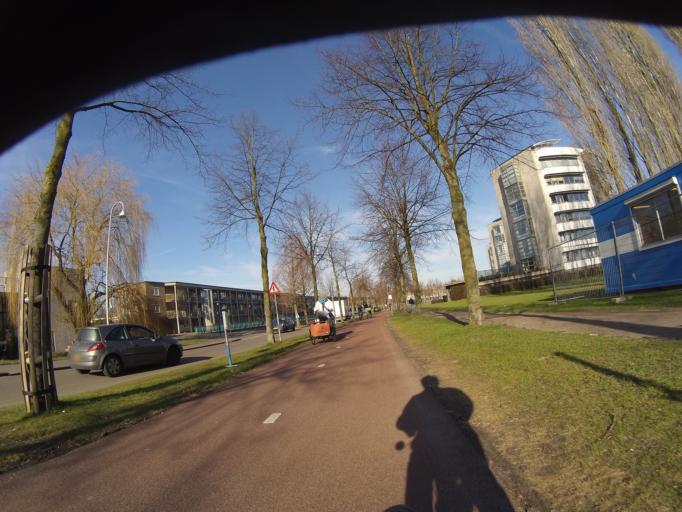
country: NL
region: Utrecht
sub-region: Gemeente Amersfoort
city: Hoogland
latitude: 52.1848
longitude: 5.3932
